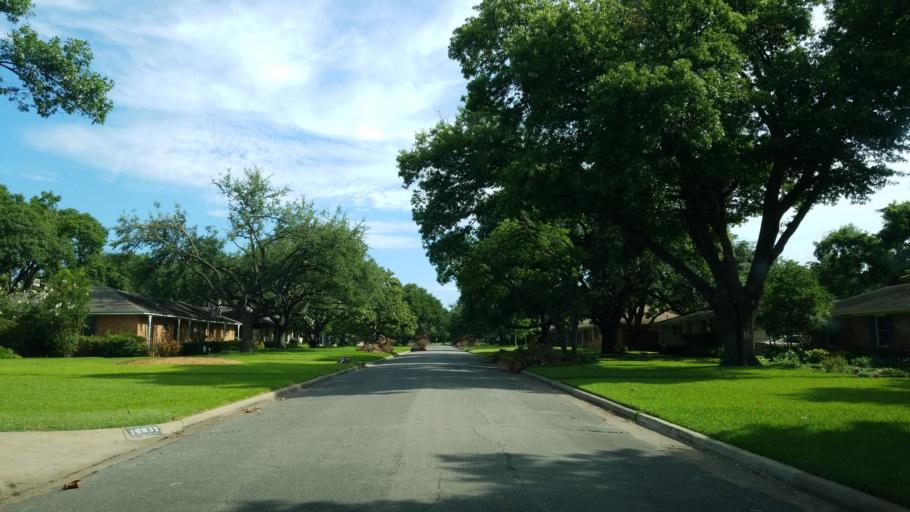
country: US
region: Texas
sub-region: Dallas County
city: Farmers Branch
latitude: 32.8965
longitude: -96.8425
